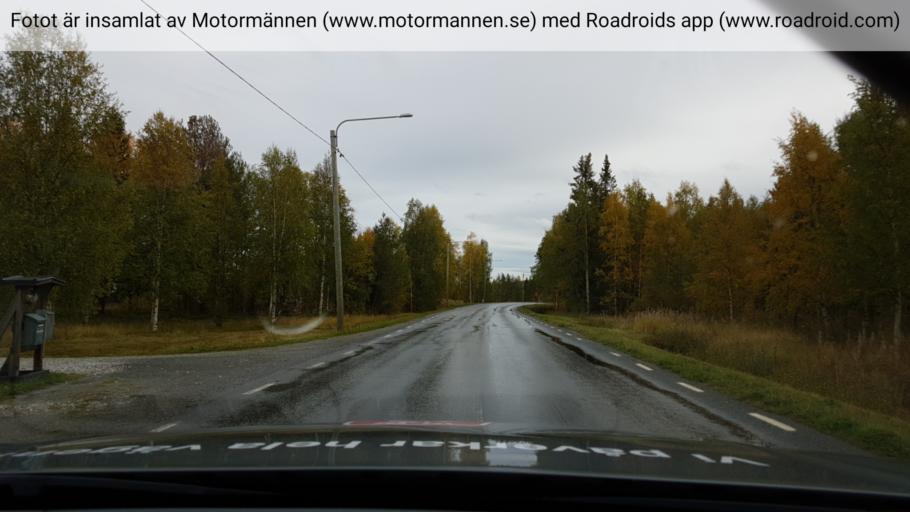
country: SE
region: Vaesterbotten
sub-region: Vilhelmina Kommun
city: Sjoberg
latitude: 64.6470
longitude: 16.3458
